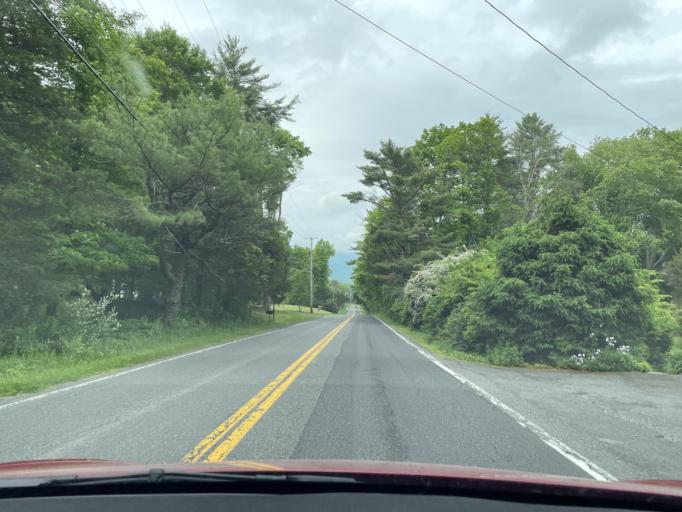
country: US
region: New York
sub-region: Ulster County
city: Zena
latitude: 42.0119
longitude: -74.0759
